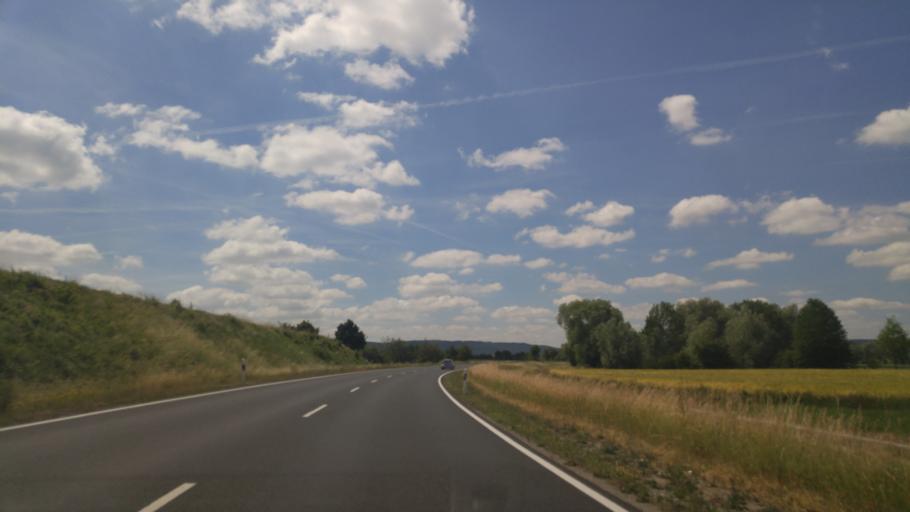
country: DE
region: Bavaria
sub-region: Regierungsbezirk Mittelfranken
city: Illesheim
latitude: 49.4770
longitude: 10.3729
